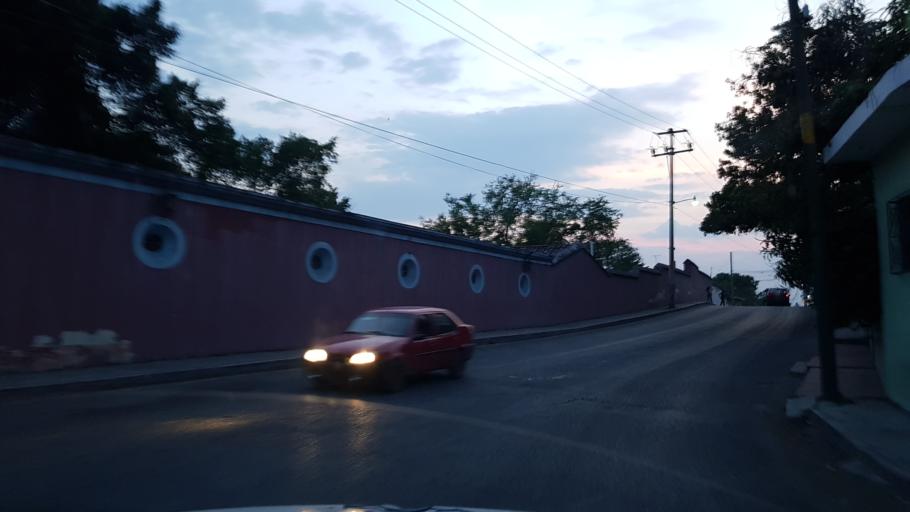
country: MX
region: Morelos
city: Tlaltizapan
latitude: 18.6876
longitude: -99.1190
